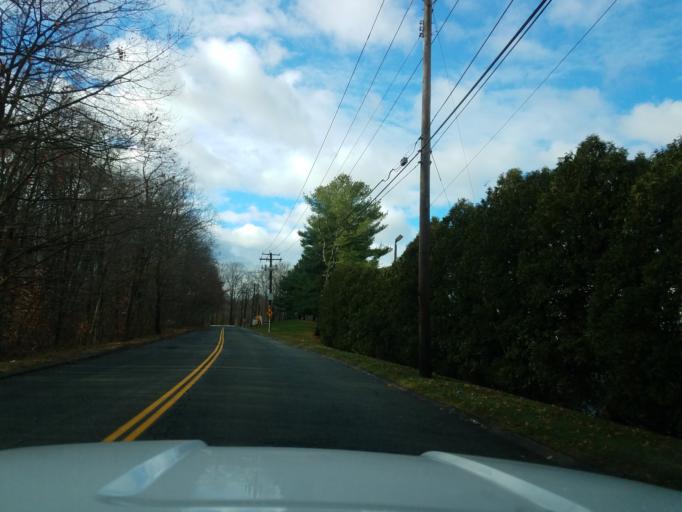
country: US
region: Connecticut
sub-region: New Haven County
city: Woodmont
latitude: 41.2297
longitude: -73.0221
